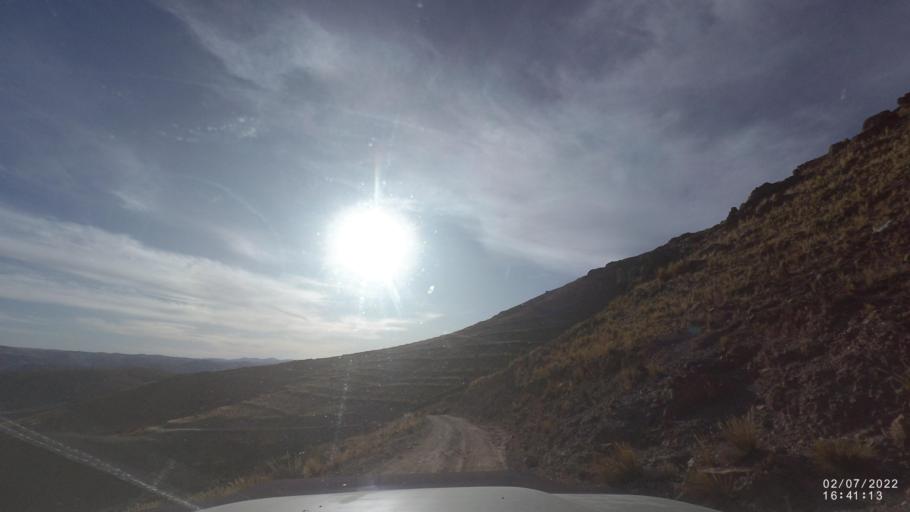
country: BO
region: Cochabamba
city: Irpa Irpa
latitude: -17.9726
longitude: -66.5004
